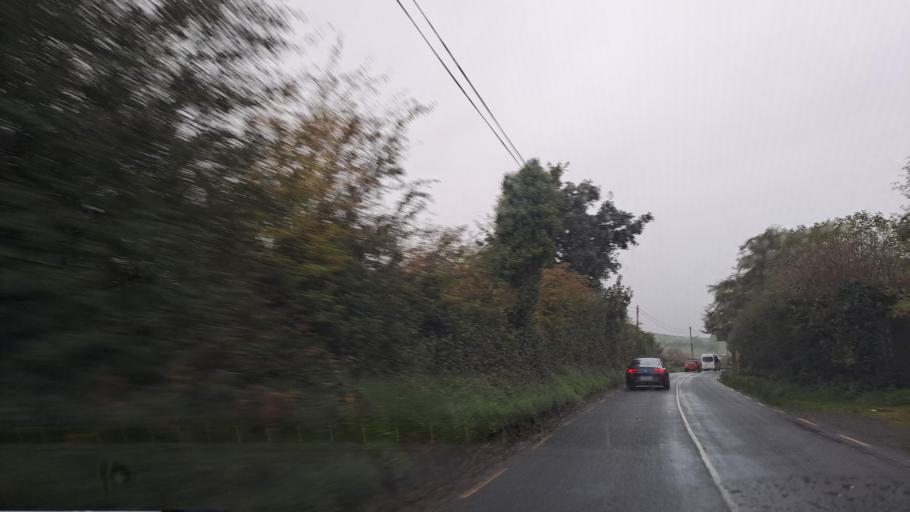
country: IE
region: Ulster
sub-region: County Monaghan
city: Monaghan
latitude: 54.2258
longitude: -6.9485
